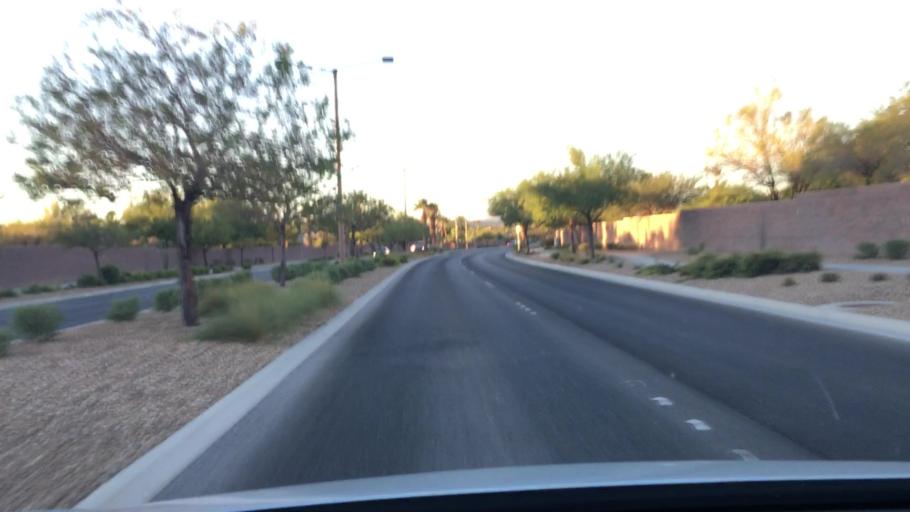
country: US
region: Nevada
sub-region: Clark County
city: Summerlin South
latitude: 36.1368
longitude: -115.3424
